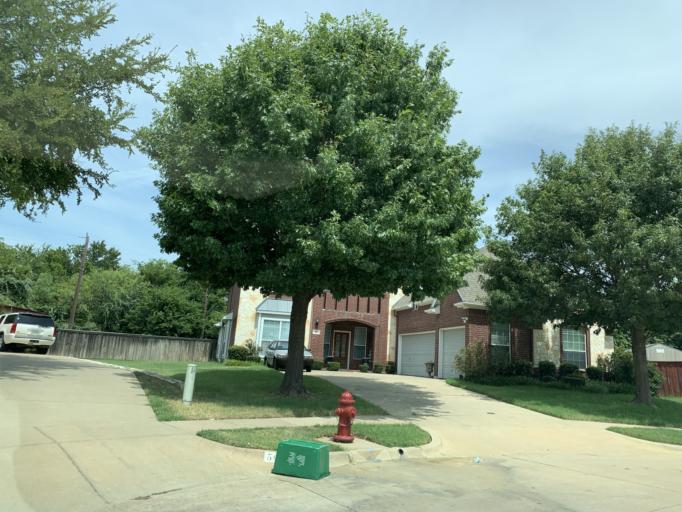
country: US
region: Texas
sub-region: Dallas County
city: Cedar Hill
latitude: 32.6527
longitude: -97.0013
